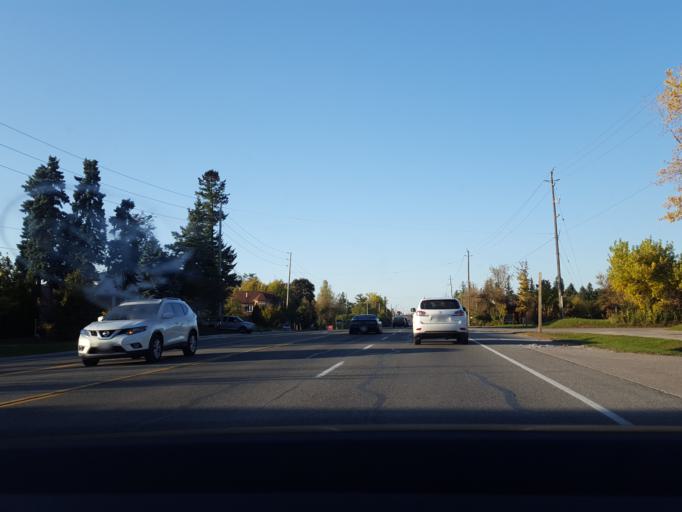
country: CA
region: Ontario
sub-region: York
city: Richmond Hill
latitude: 43.9184
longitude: -79.4483
